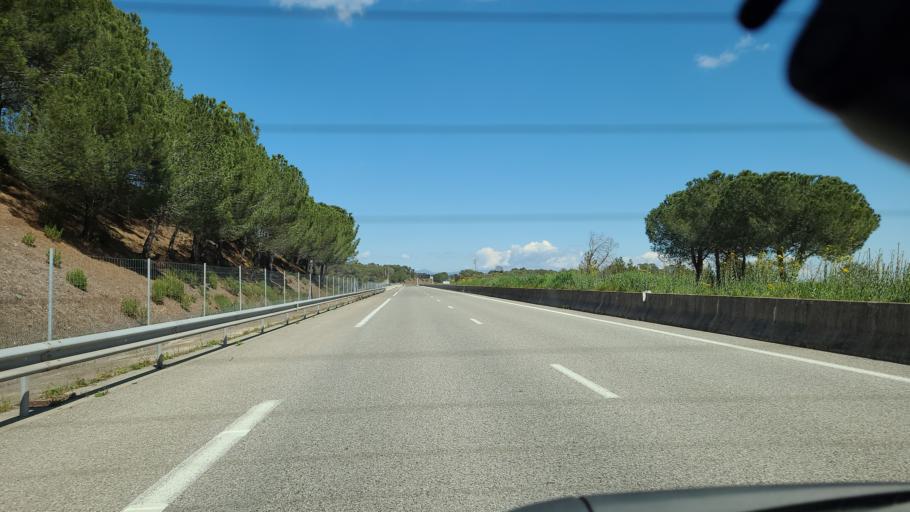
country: FR
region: Provence-Alpes-Cote d'Azur
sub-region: Departement du Var
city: Le Cannet-des-Maures
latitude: 43.3687
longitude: 6.3436
